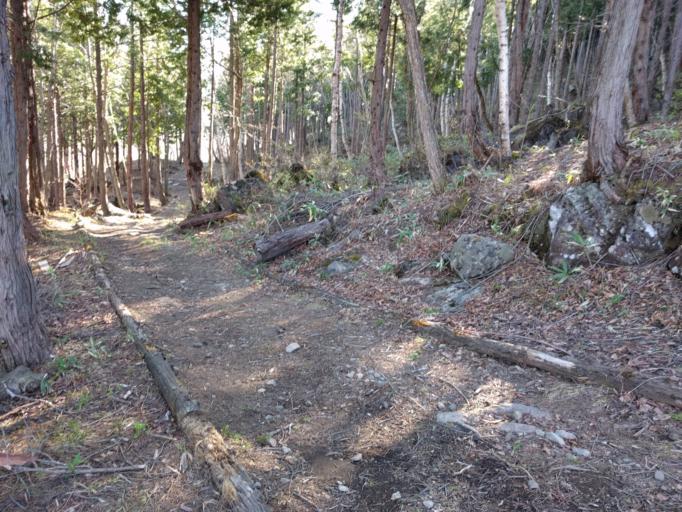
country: JP
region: Nagano
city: Nakano
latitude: 36.7211
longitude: 138.4792
